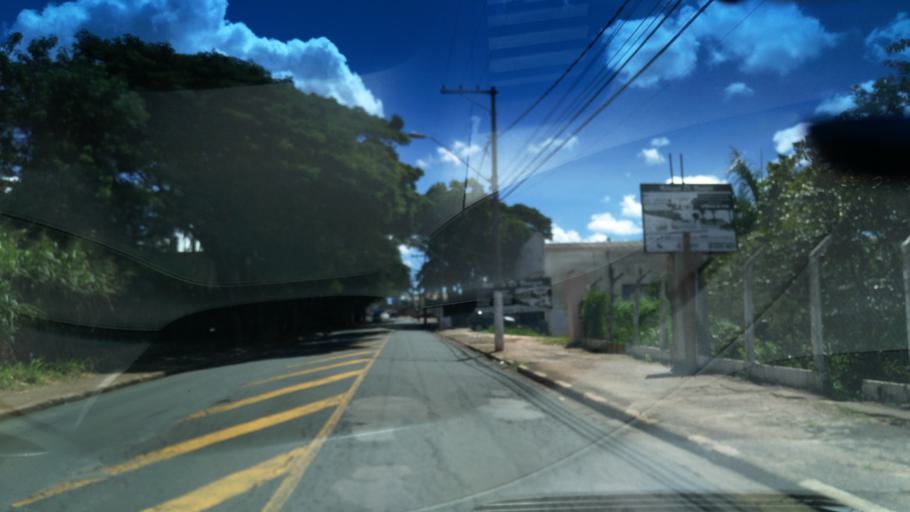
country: BR
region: Sao Paulo
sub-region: Valinhos
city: Valinhos
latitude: -22.9583
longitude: -47.0057
